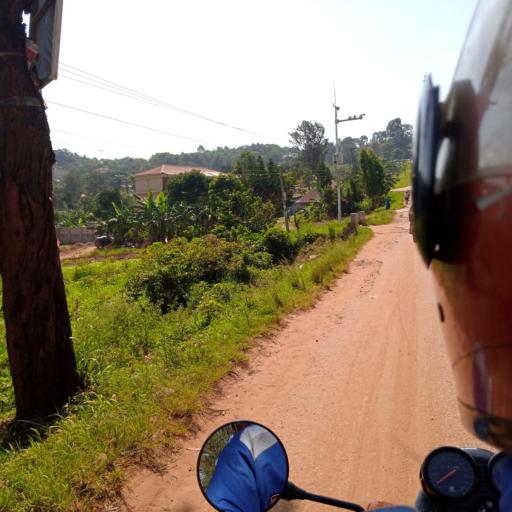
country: UG
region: Central Region
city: Masaka
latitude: -0.3434
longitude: 31.7305
